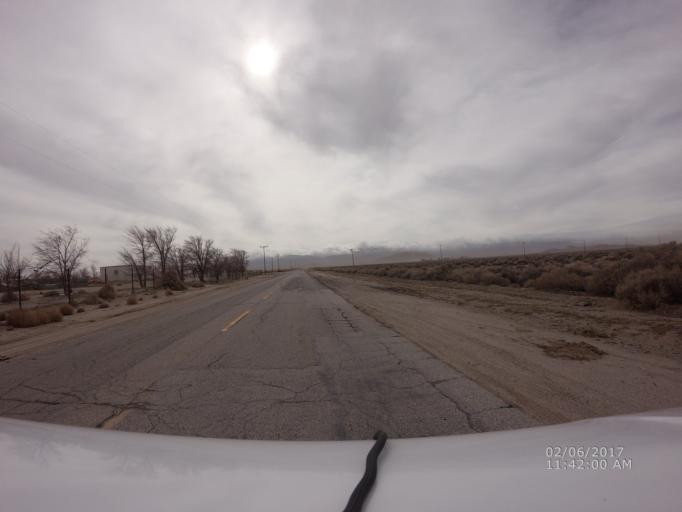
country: US
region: California
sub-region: Los Angeles County
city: Lake Los Angeles
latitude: 34.6033
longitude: -117.7025
